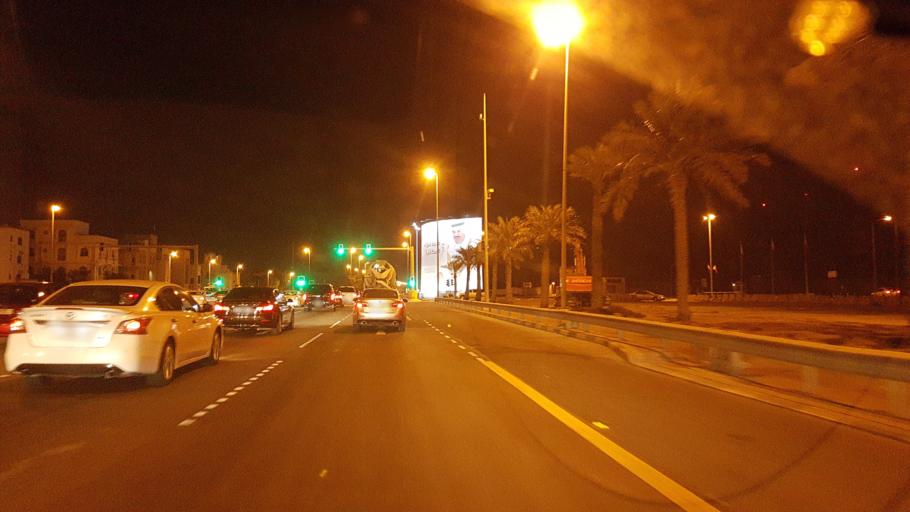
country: BH
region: Muharraq
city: Al Hadd
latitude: 26.2331
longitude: 50.6579
